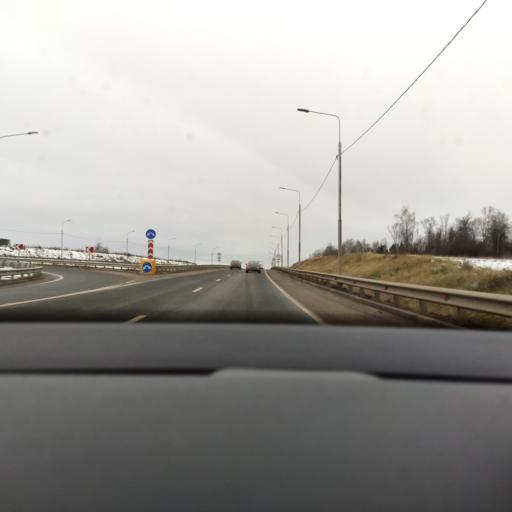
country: RU
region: Moskovskaya
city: Bol'shiye Vyazemy
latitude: 55.6415
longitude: 36.9950
